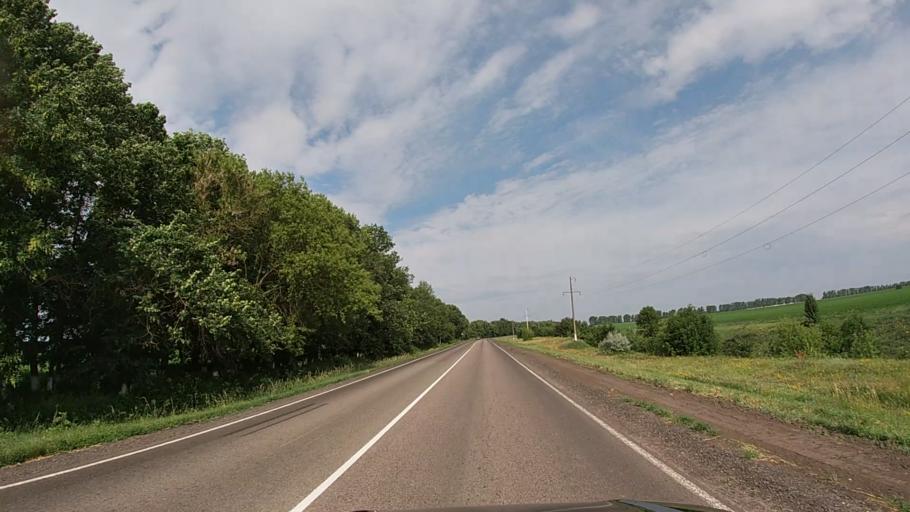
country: RU
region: Belgorod
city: Krasnaya Yaruga
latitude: 50.8013
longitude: 35.5610
